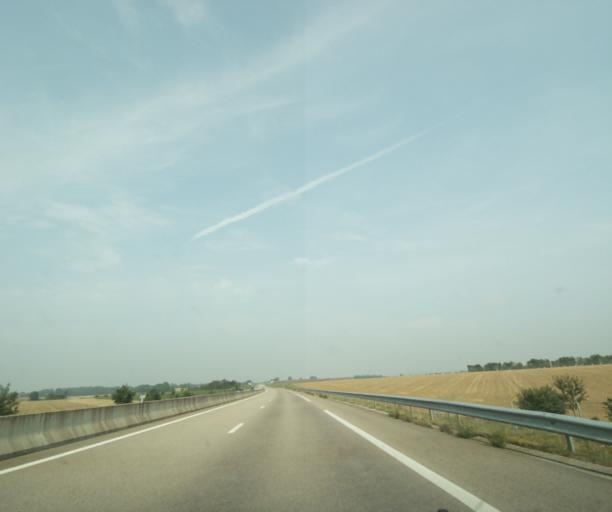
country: FR
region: Lower Normandy
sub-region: Departement de l'Orne
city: Ecouche
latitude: 48.7703
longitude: -0.1017
